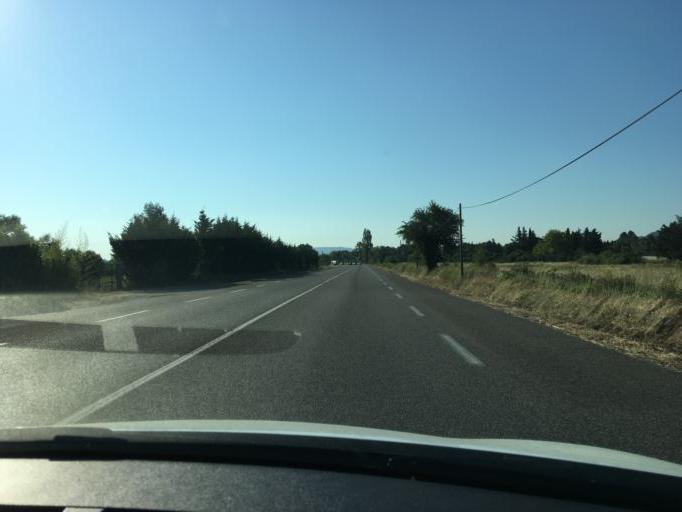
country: FR
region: Provence-Alpes-Cote d'Azur
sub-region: Departement des Bouches-du-Rhone
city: Alleins
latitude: 43.7318
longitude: 5.1406
